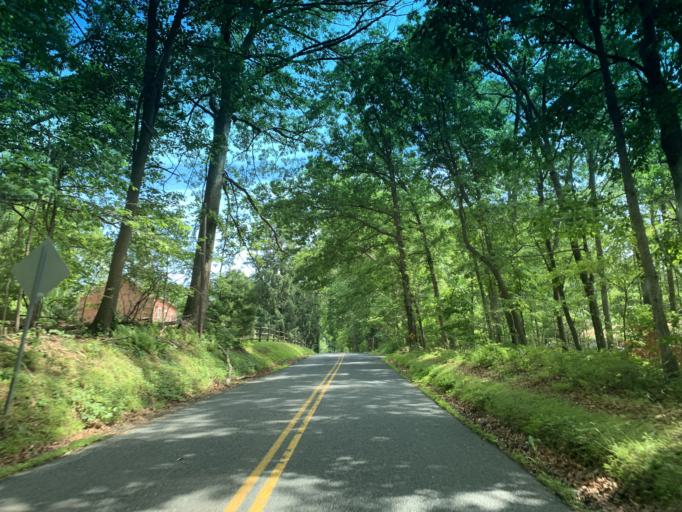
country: US
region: Maryland
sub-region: Harford County
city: Jarrettsville
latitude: 39.6502
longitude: -76.4409
